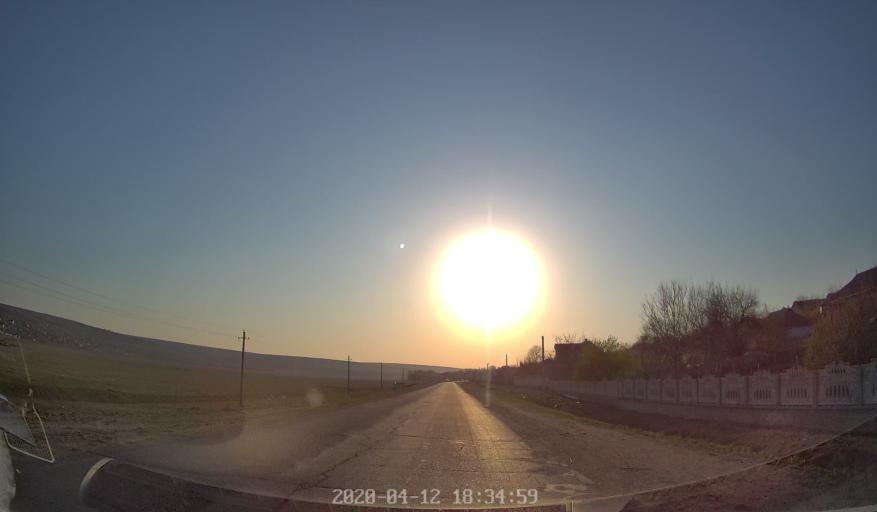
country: MD
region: Chisinau
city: Vadul lui Voda
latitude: 47.1169
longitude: 29.0542
